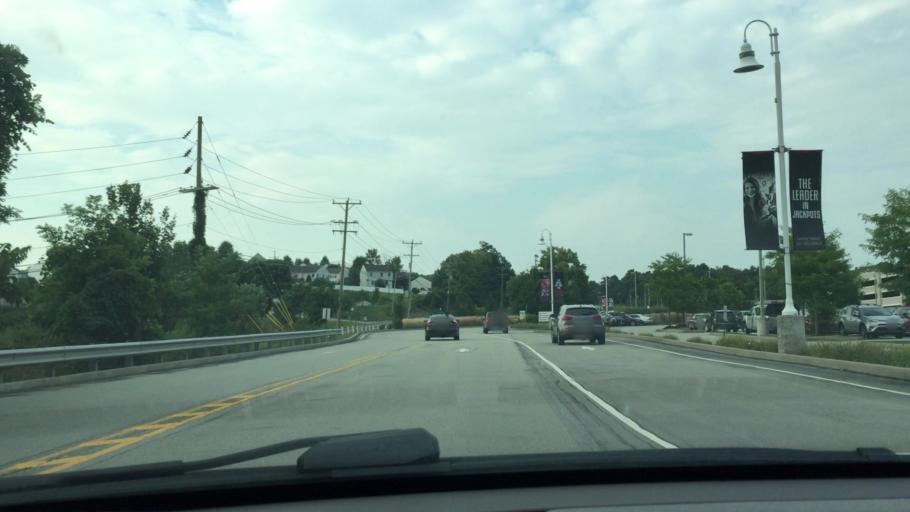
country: US
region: Pennsylvania
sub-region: Washington County
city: McGovern
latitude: 40.2203
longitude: -80.2037
